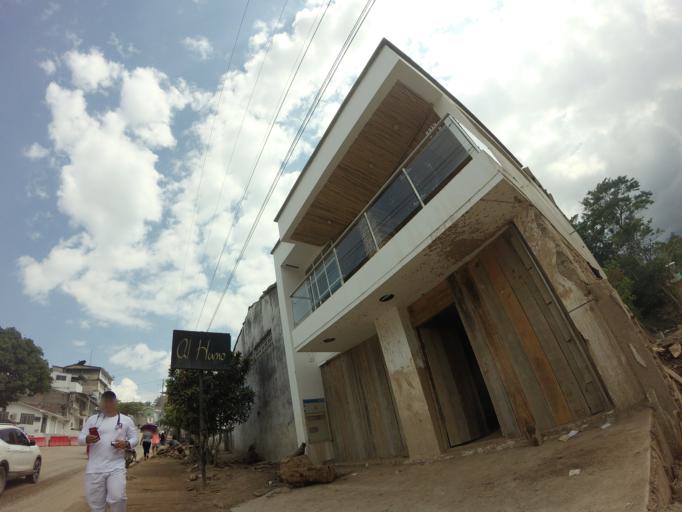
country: CO
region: Putumayo
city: Mocoa
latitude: 1.1488
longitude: -76.6484
